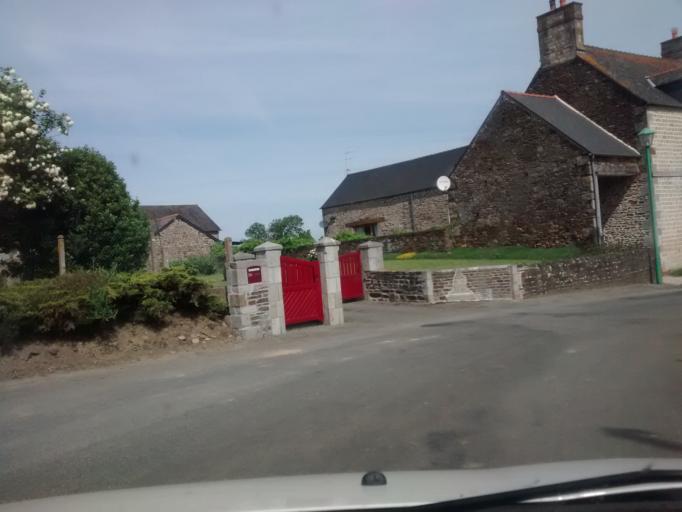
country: FR
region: Lower Normandy
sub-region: Departement de la Manche
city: Pontorson
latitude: 48.5100
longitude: -1.5239
